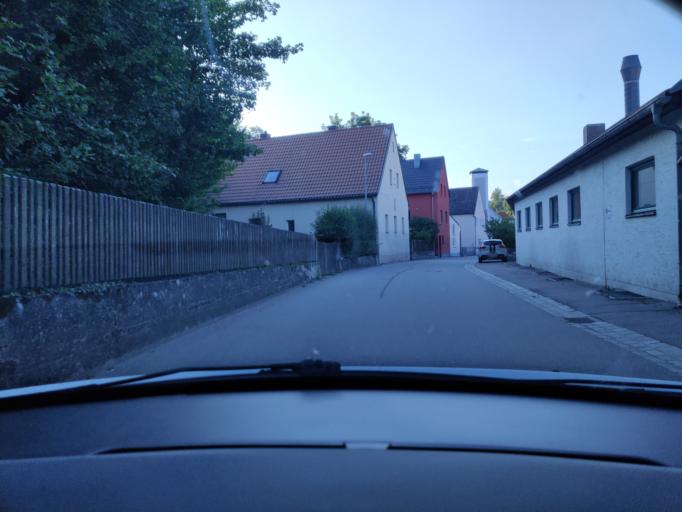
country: DE
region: Bavaria
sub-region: Upper Palatinate
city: Nabburg
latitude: 49.4530
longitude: 12.1787
